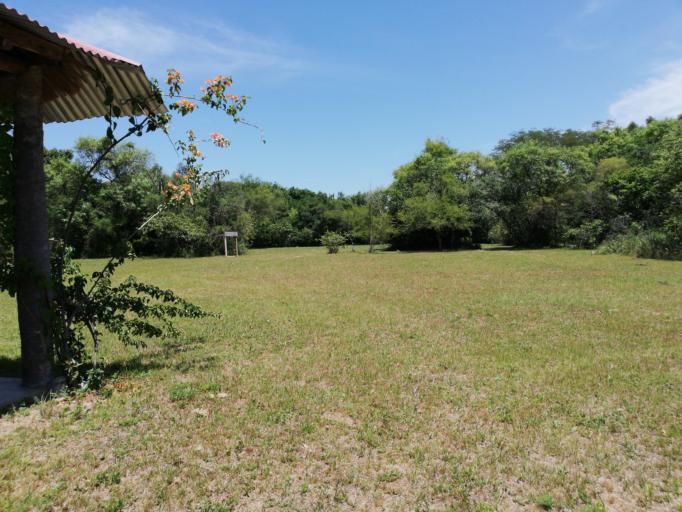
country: AR
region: Corrientes
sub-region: Departamento de San Miguel
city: San Miguel
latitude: -27.9880
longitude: -57.5407
